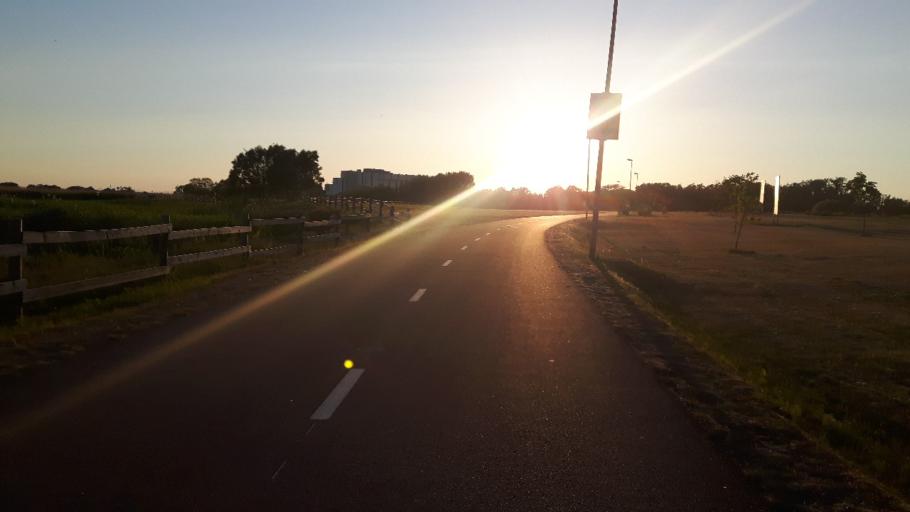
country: EE
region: Paernumaa
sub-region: Paernu linn
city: Parnu
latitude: 58.3705
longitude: 24.5227
